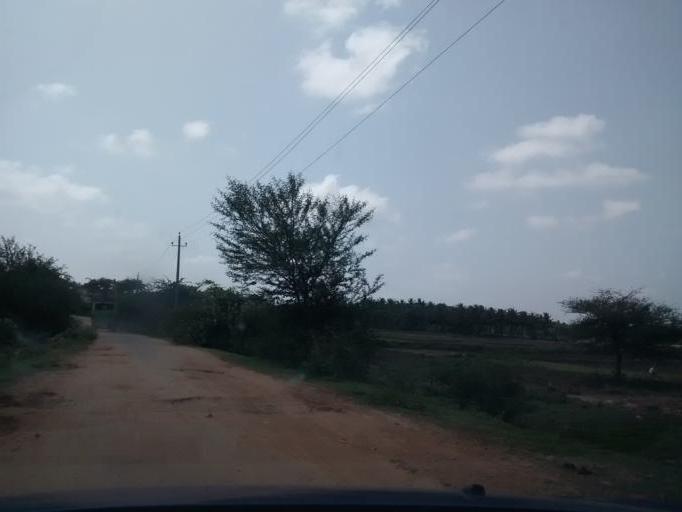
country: IN
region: Karnataka
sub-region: Hassan
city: Hole Narsipur
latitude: 12.6929
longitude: 76.1832
